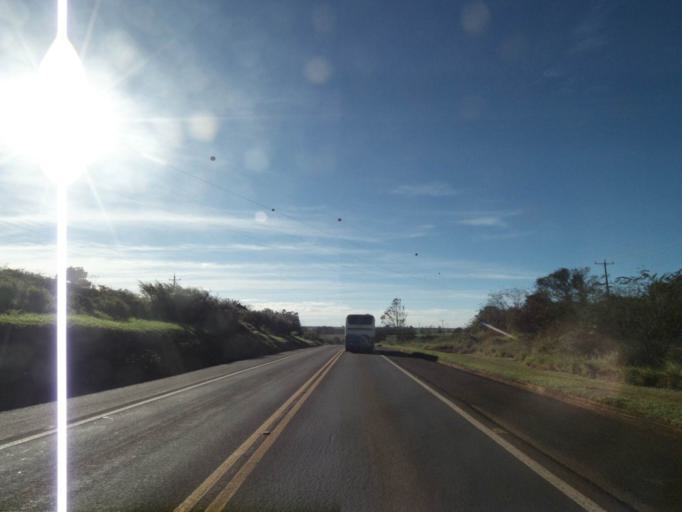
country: BR
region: Parana
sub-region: Cascavel
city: Cascavel
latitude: -25.0291
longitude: -53.5706
